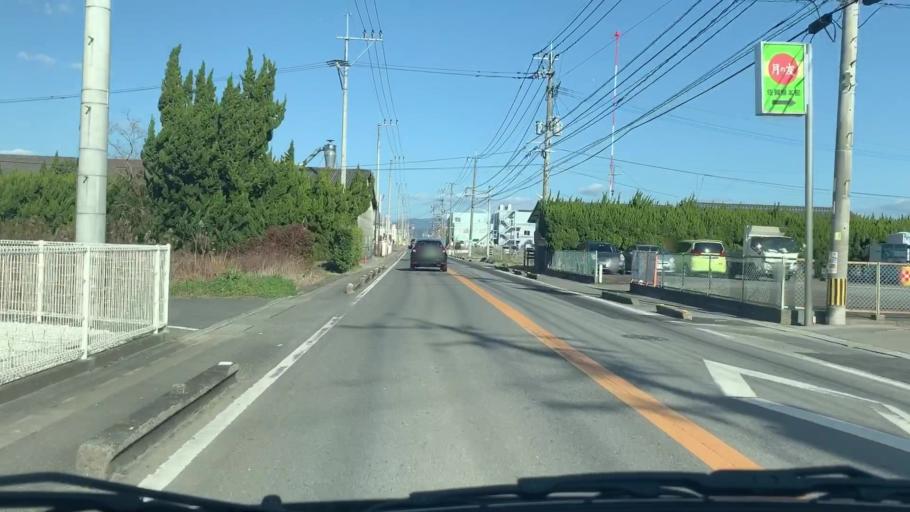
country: JP
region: Saga Prefecture
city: Saga-shi
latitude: 33.2484
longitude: 130.2654
